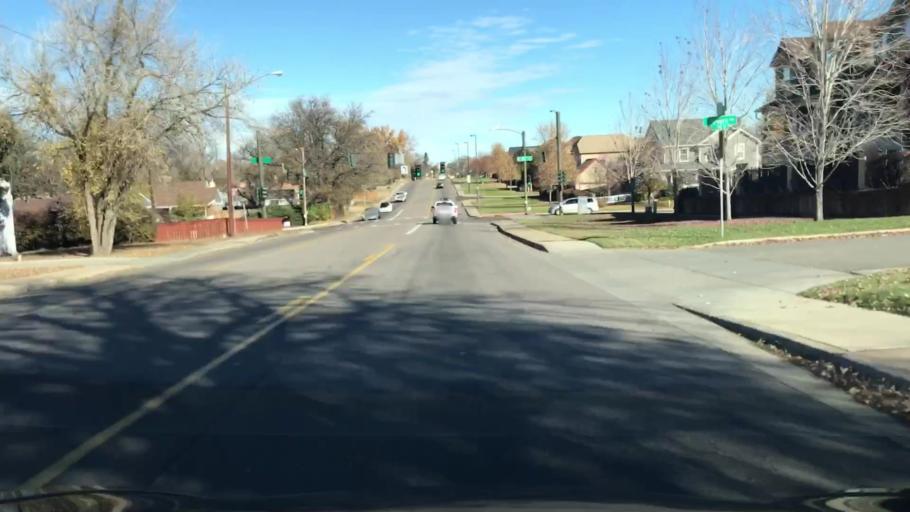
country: US
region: Colorado
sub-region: Arapahoe County
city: Glendale
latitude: 39.7286
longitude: -104.9035
